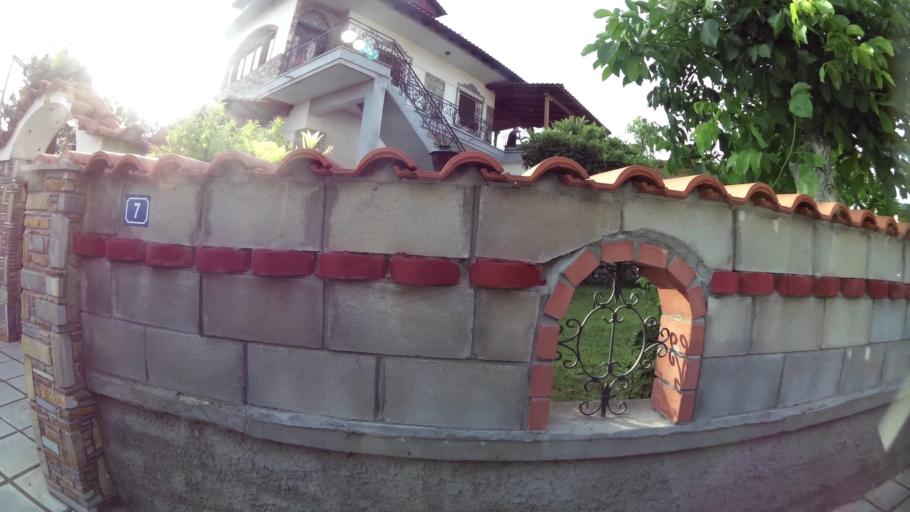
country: GR
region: Central Macedonia
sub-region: Nomos Thessalonikis
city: Oraiokastro
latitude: 40.7225
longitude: 22.9066
